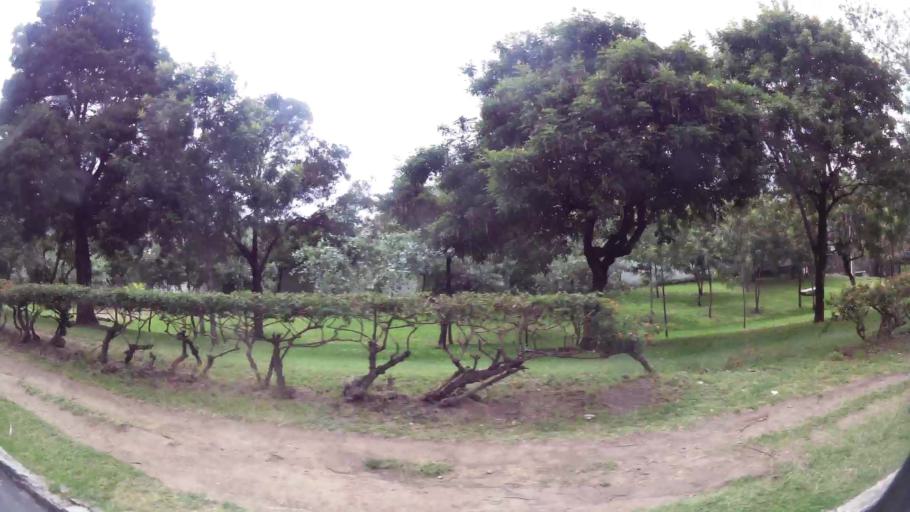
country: EC
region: Pichincha
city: Quito
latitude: -0.1623
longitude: -78.4930
